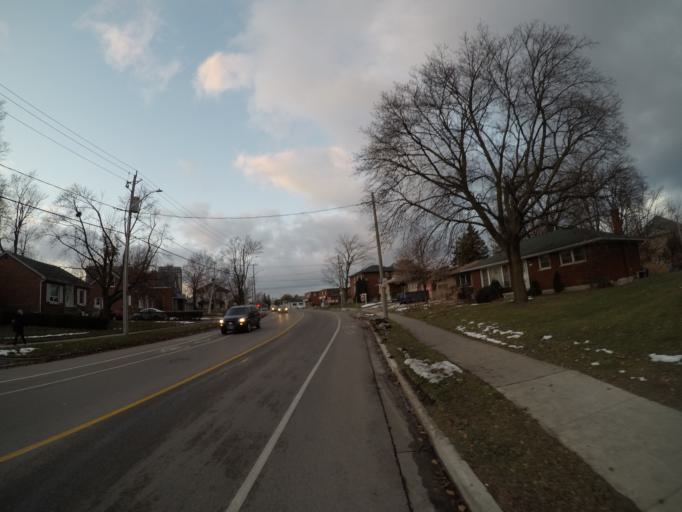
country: CA
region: Ontario
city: Waterloo
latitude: 43.4617
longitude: -80.4931
